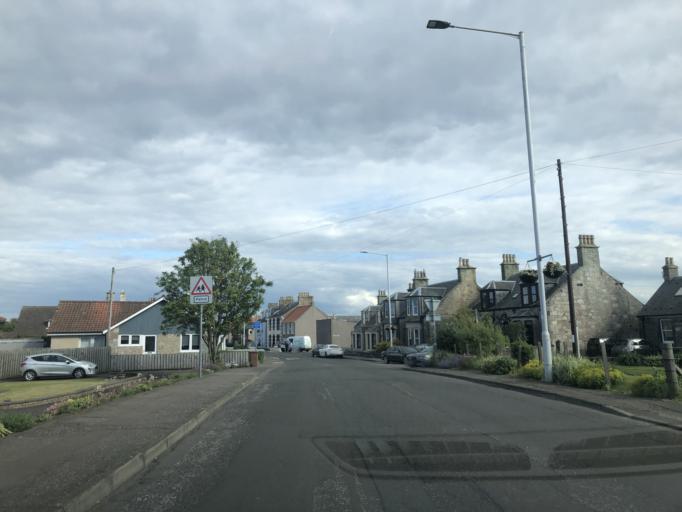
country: GB
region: Scotland
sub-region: Fife
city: Saint Monance
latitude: 56.2076
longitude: -2.7682
